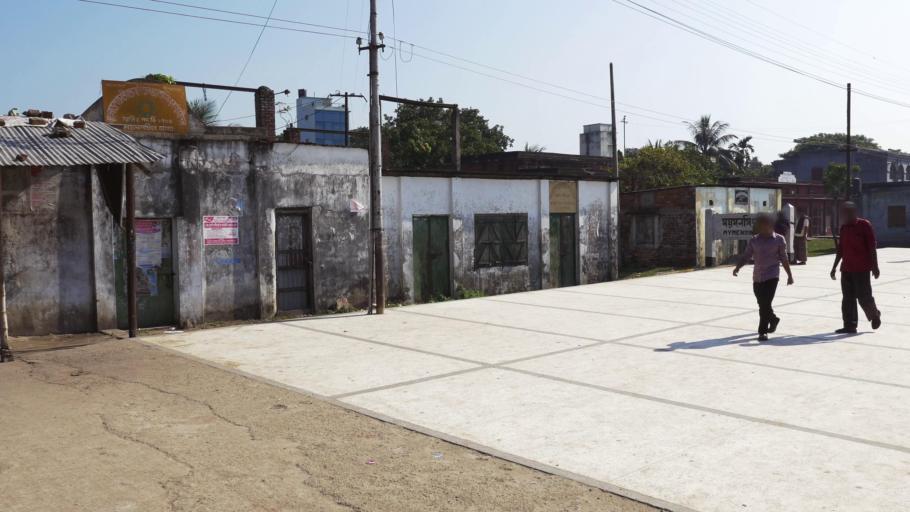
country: BD
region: Dhaka
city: Mymensingh
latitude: 24.6968
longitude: 90.4515
